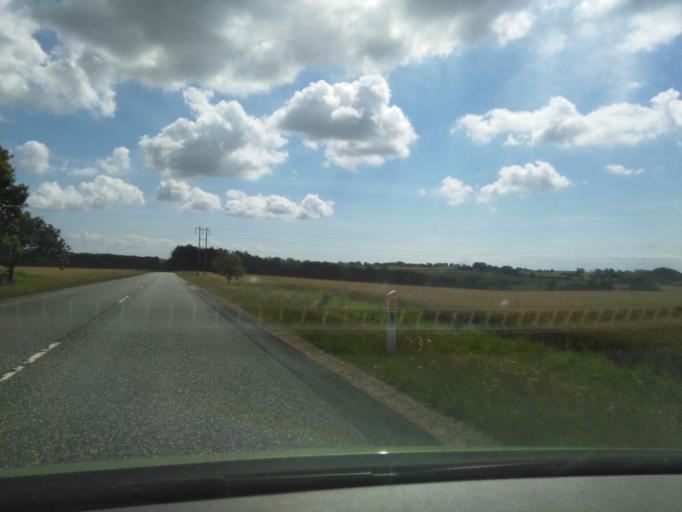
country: DK
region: Central Jutland
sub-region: Odder Kommune
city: Odder
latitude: 55.9654
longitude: 10.0947
